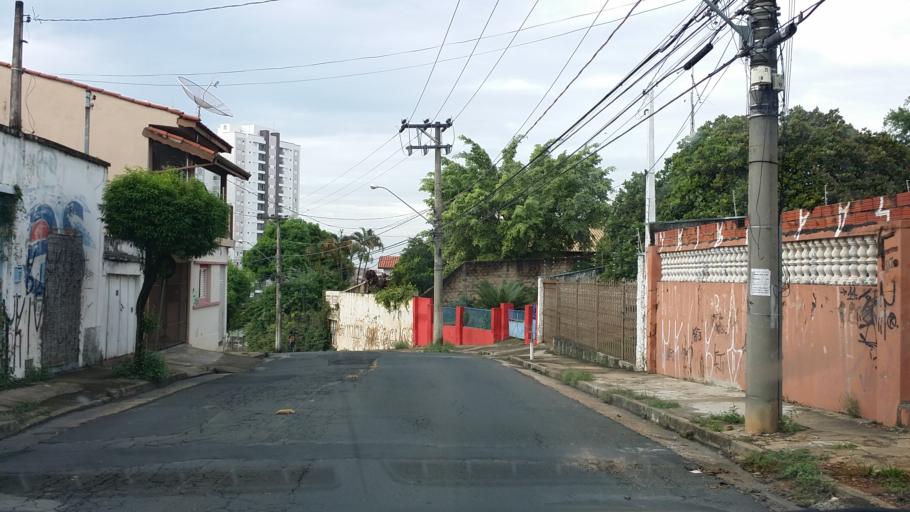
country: BR
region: Sao Paulo
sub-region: Indaiatuba
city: Indaiatuba
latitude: -23.0924
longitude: -47.2183
